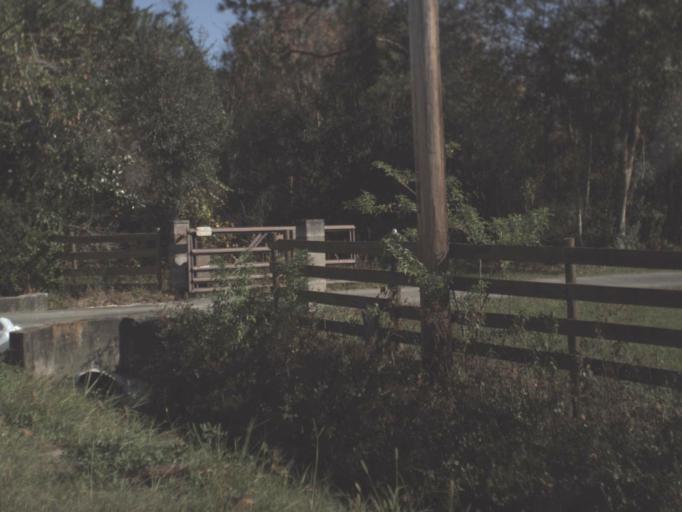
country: US
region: Florida
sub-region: Volusia County
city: Samsula-Spruce Creek
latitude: 29.0825
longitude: -81.0700
